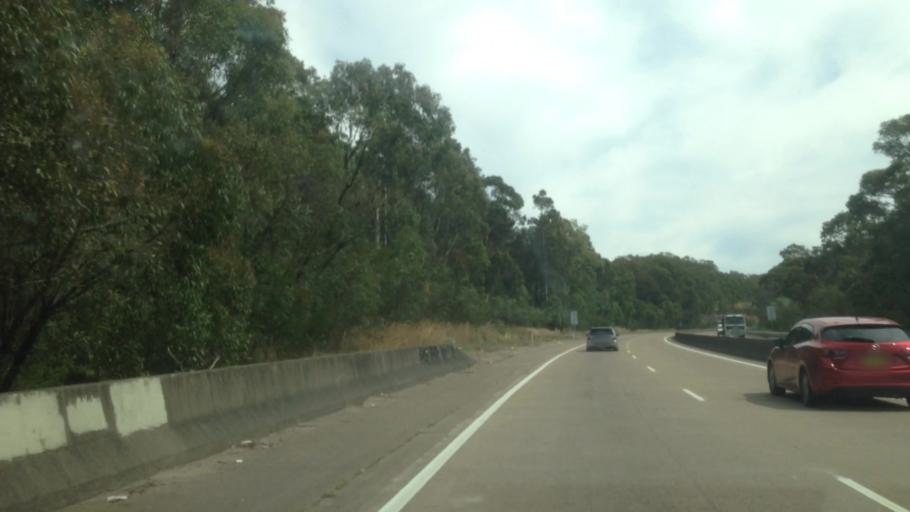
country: AU
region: New South Wales
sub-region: Newcastle
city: Elermore Vale
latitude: -32.9103
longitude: 151.6554
